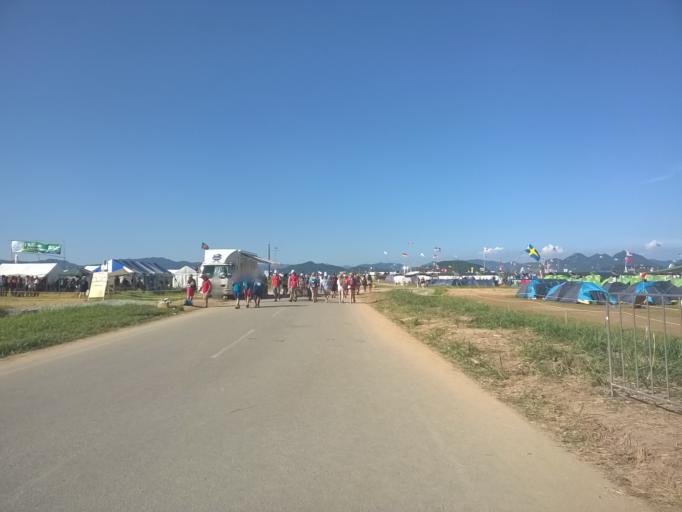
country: JP
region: Yamaguchi
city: Ogori-shimogo
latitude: 34.0146
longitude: 131.3708
